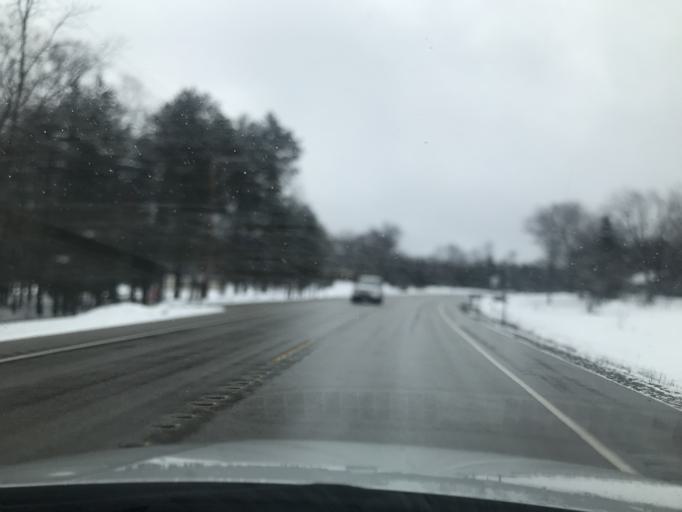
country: US
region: Wisconsin
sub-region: Marinette County
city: Peshtigo
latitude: 45.1685
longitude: -87.7318
